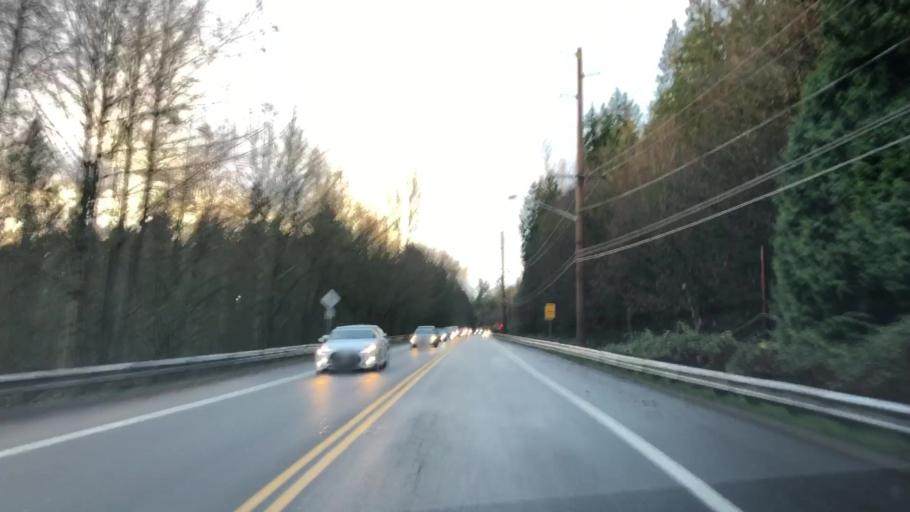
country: US
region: Washington
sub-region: King County
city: Sammamish
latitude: 47.6482
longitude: -122.0559
